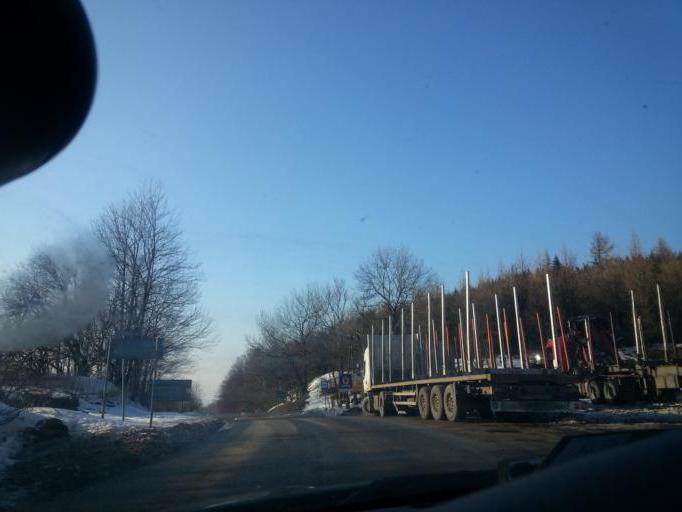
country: PL
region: Lower Silesian Voivodeship
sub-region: Powiat jeleniogorski
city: Kowary
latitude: 50.7626
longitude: 15.8676
